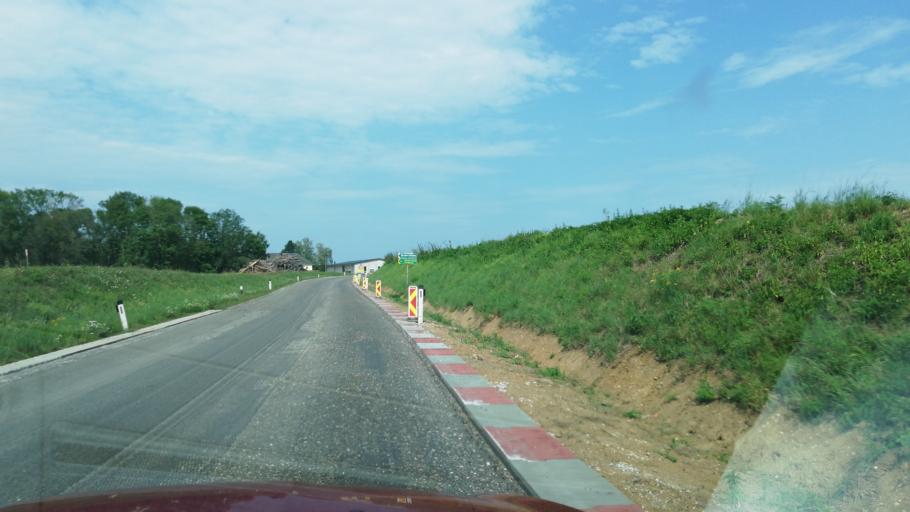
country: AT
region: Upper Austria
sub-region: Politischer Bezirk Steyr-Land
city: Sierning
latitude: 48.1094
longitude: 14.3237
